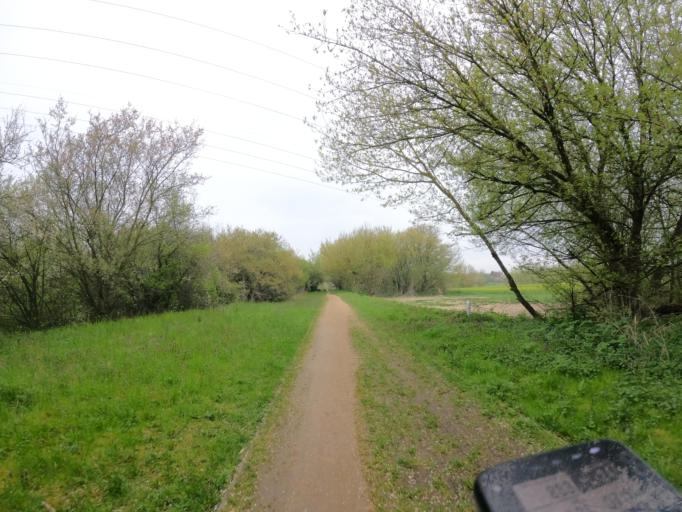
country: DE
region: Berlin
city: Gropiusstadt
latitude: 52.3782
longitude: 13.4564
